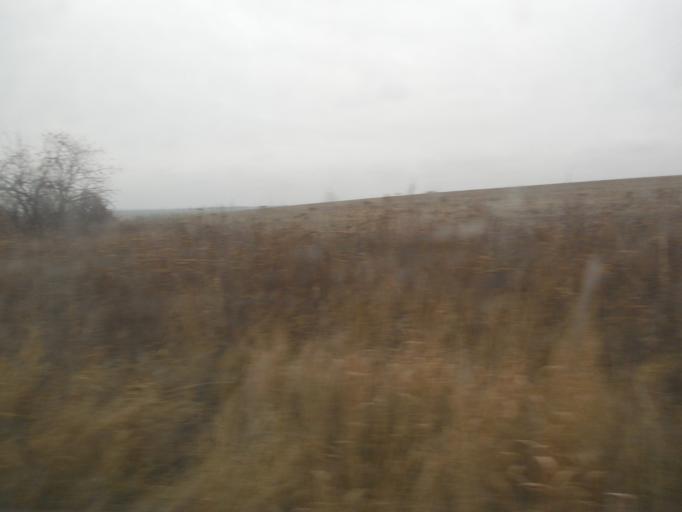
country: RU
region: Lipetsk
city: Donskoye
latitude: 52.6043
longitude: 38.9111
